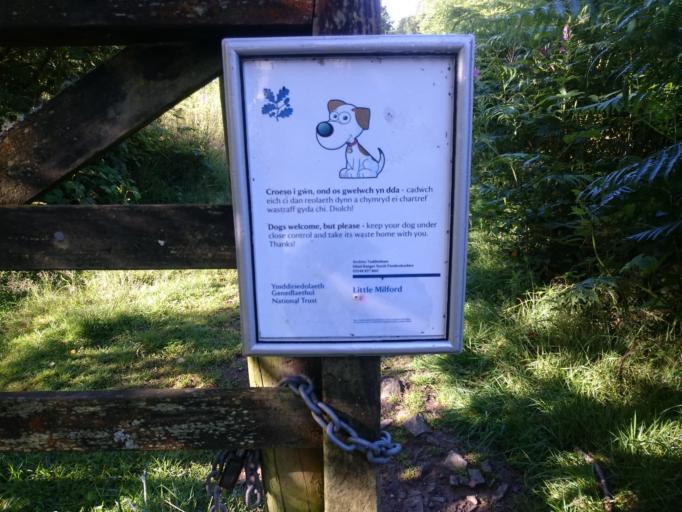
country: GB
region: Wales
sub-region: Pembrokeshire
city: Freystrop
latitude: 51.7691
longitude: -4.9518
